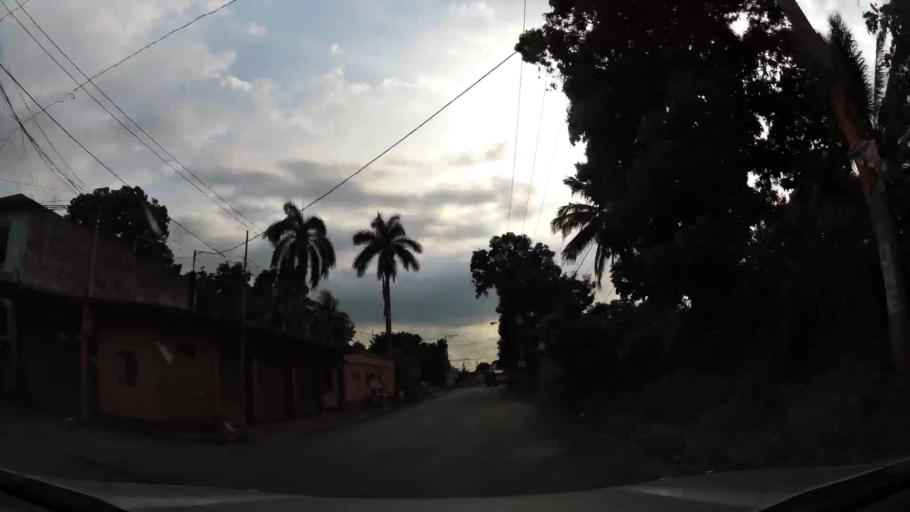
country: GT
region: Escuintla
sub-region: Municipio de Escuintla
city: Escuintla
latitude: 14.3078
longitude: -90.7820
